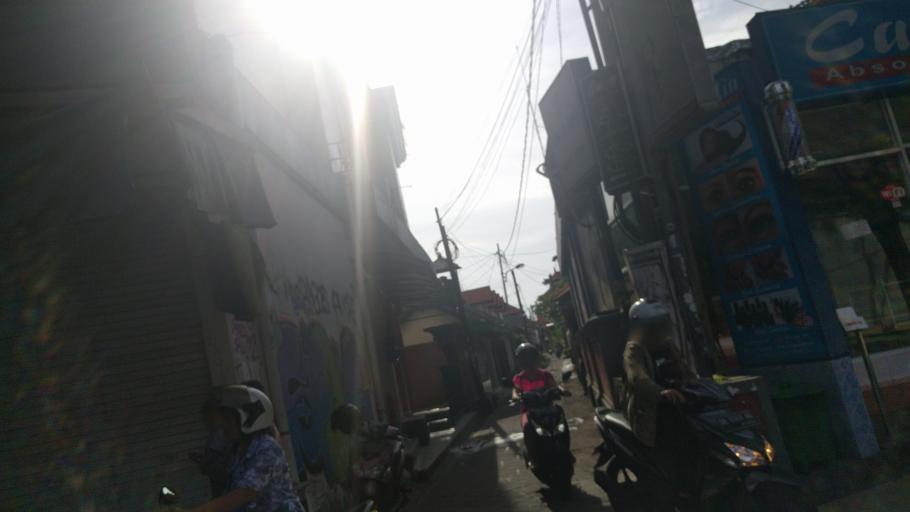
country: ID
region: Bali
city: Kuta
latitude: -8.7208
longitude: 115.1752
